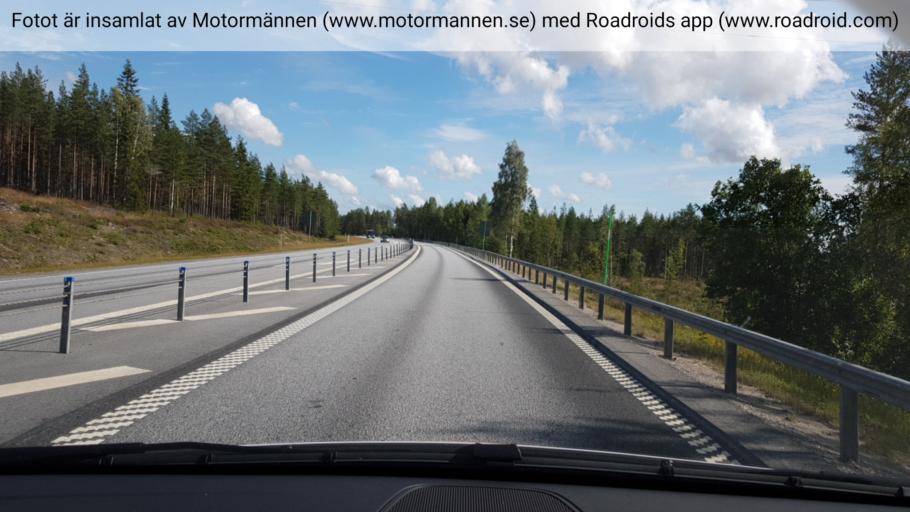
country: SE
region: Vaesterbotten
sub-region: Vannas Kommun
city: Vannasby
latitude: 63.8888
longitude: 19.9992
